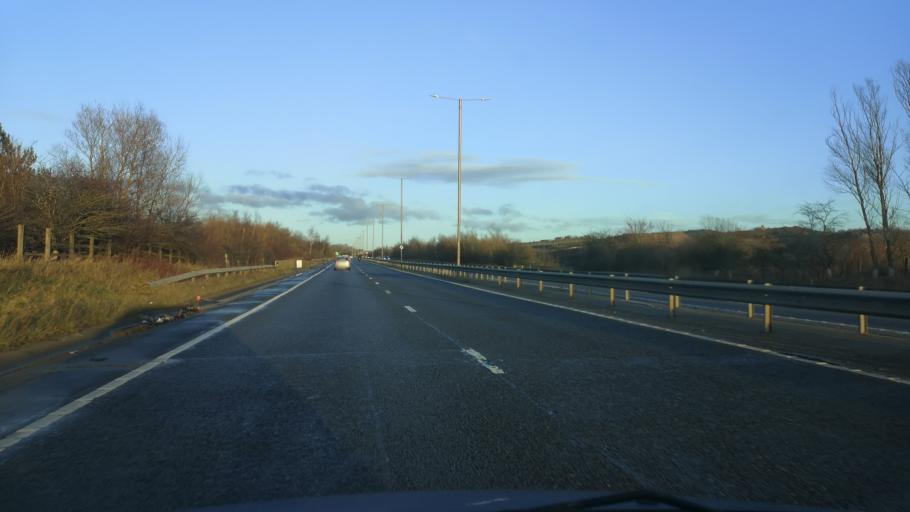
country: GB
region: England
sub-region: Barnsley
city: Birdwell
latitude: 53.5039
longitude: -1.4694
